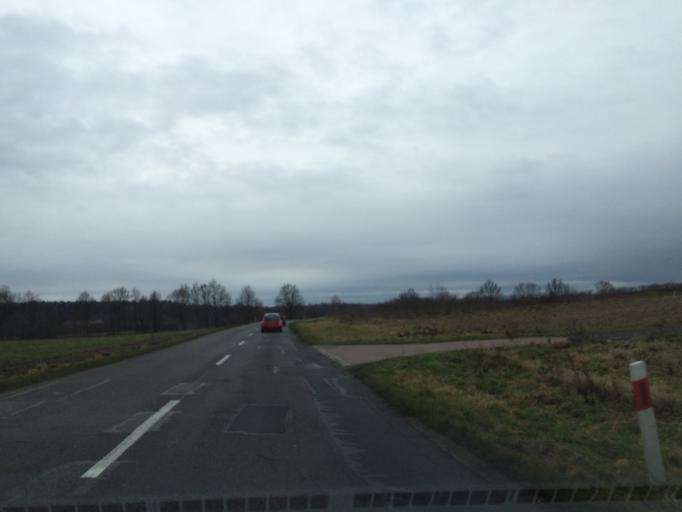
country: PL
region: Lower Silesian Voivodeship
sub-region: Powiat lwowecki
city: Lwowek Slaski
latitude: 51.1825
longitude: 15.5662
